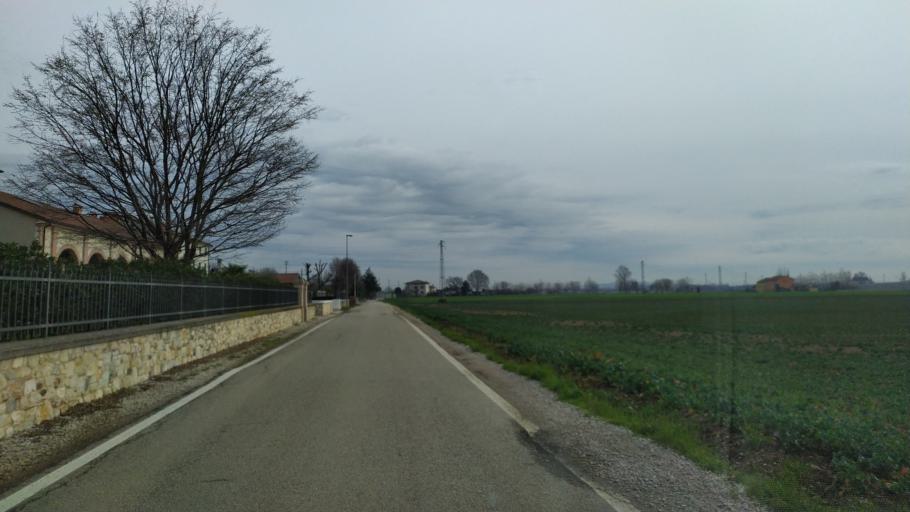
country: IT
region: Veneto
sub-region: Provincia di Vicenza
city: Isola Vicentina
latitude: 45.6524
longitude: 11.4603
